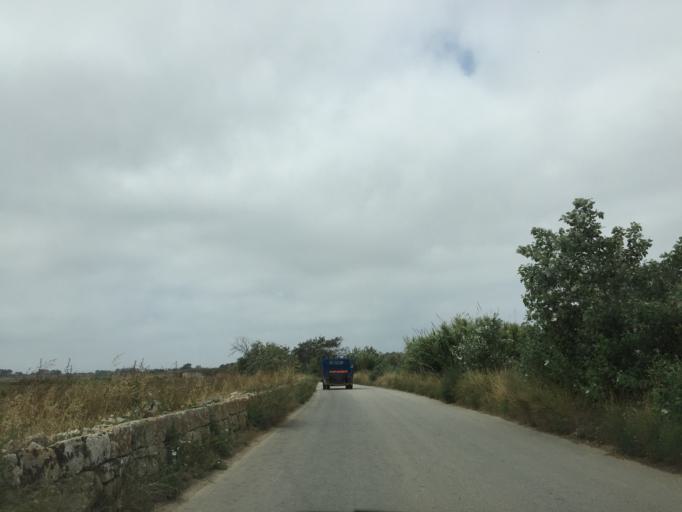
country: MT
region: Ir-Rabat
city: Rabat
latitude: 35.8850
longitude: 14.3780
